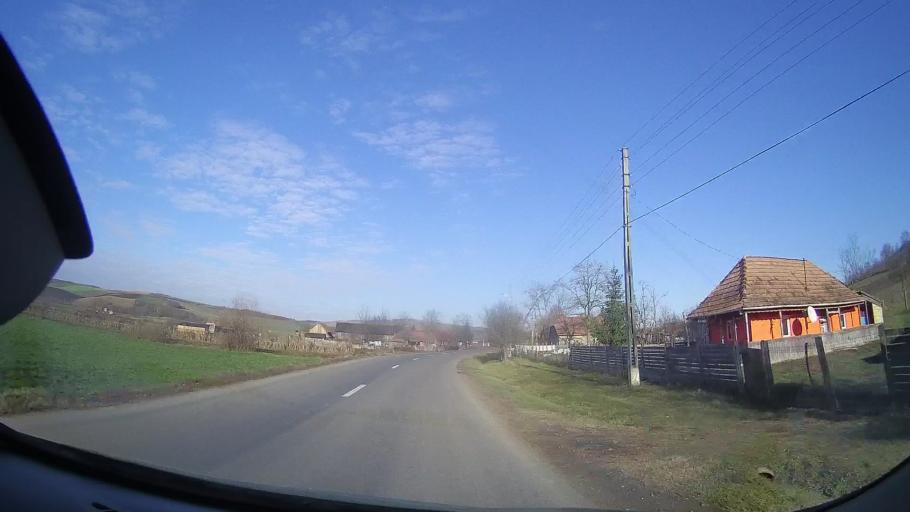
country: RO
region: Mures
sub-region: Comuna Band
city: Band
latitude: 46.5564
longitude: 24.3352
